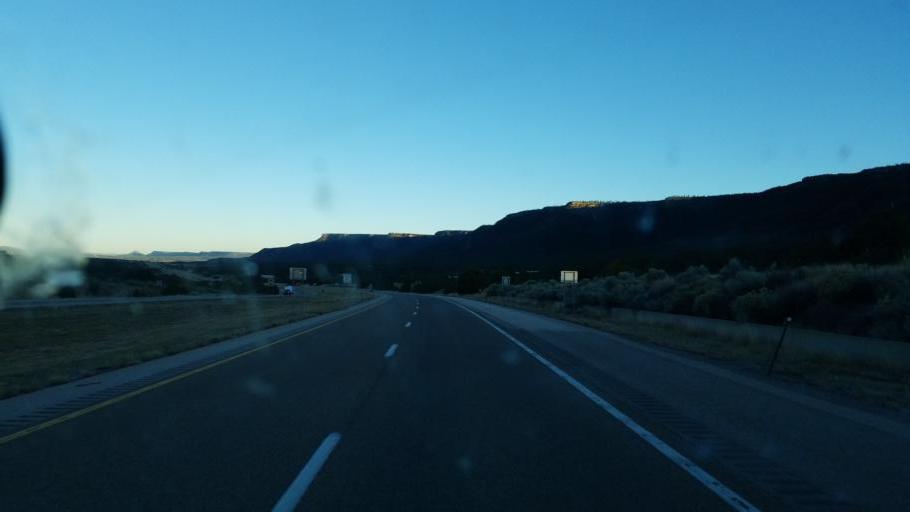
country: US
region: New Mexico
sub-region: San Miguel County
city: Pecos
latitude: 35.4312
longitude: -105.6004
